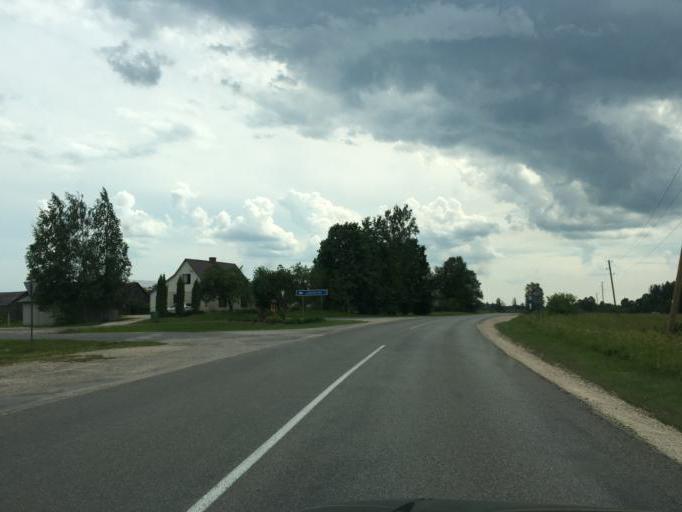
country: LV
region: Rugaju
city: Rugaji
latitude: 56.9188
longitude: 27.0714
